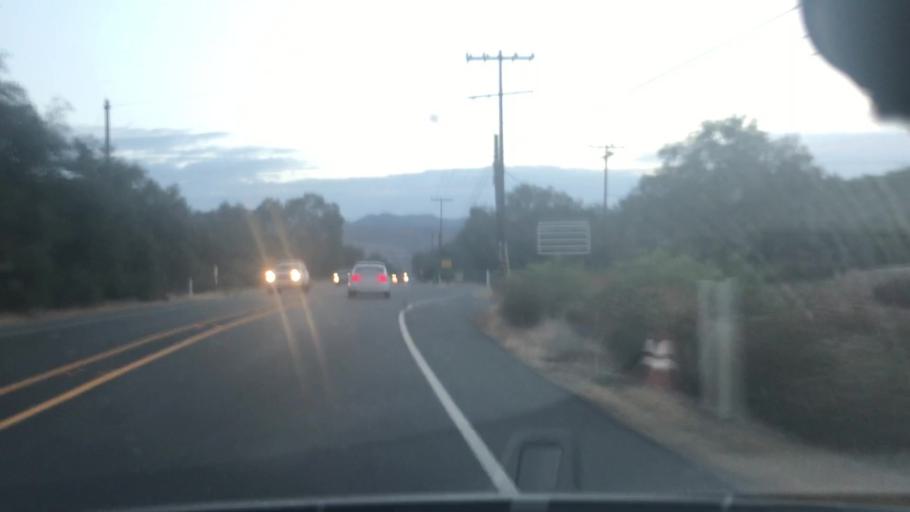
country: US
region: California
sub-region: Orange County
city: Coto De Caza
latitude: 33.5570
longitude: -117.5489
